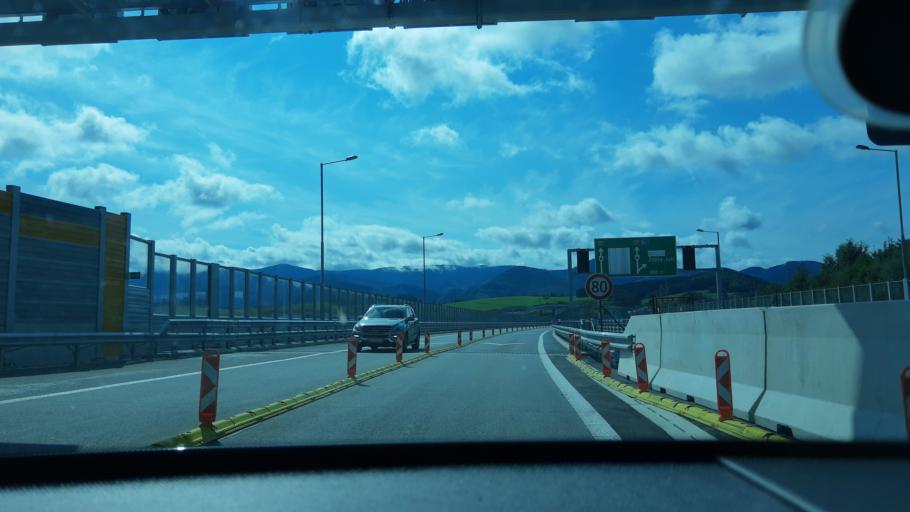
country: SK
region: Zilinsky
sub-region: Okres Zilina
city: Zilina
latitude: 49.1857
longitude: 18.7206
